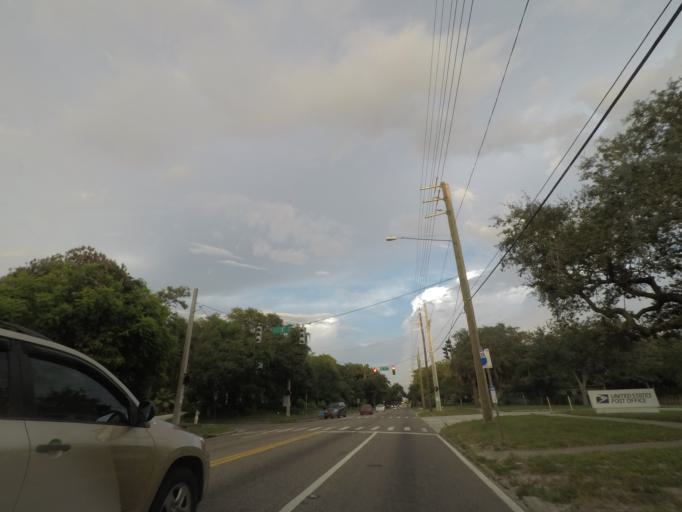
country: US
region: Florida
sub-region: Pinellas County
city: Gulfport
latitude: 27.7483
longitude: -82.6913
